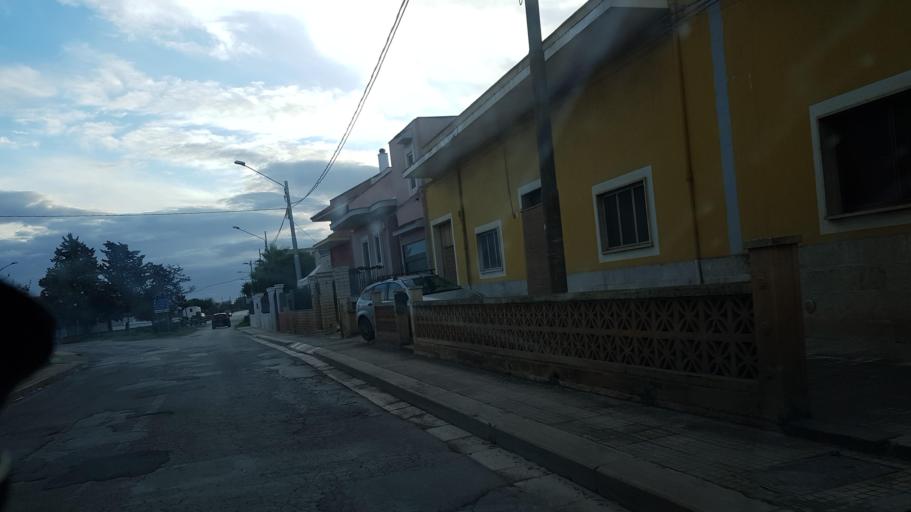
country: IT
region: Apulia
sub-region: Provincia di Brindisi
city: San Vito dei Normanni
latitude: 40.6524
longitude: 17.7007
